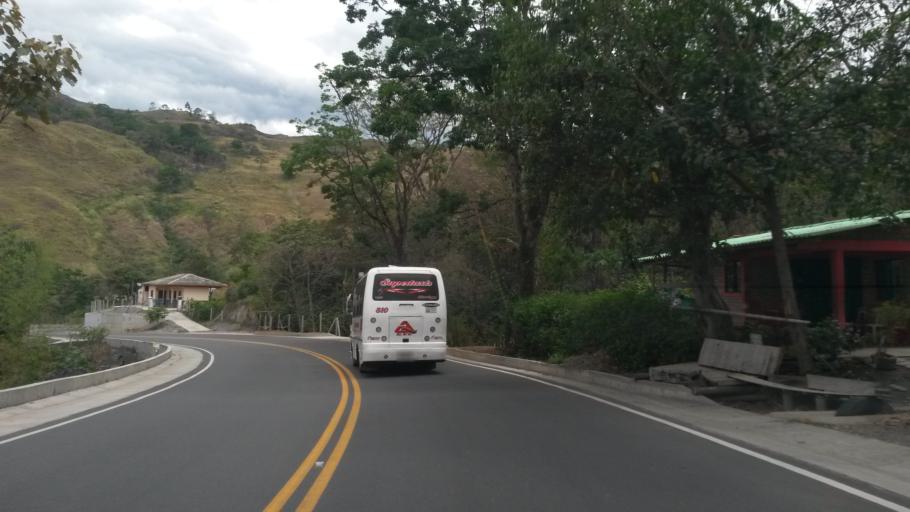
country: CO
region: Cauca
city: Rosas
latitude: 2.2798
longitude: -76.7118
